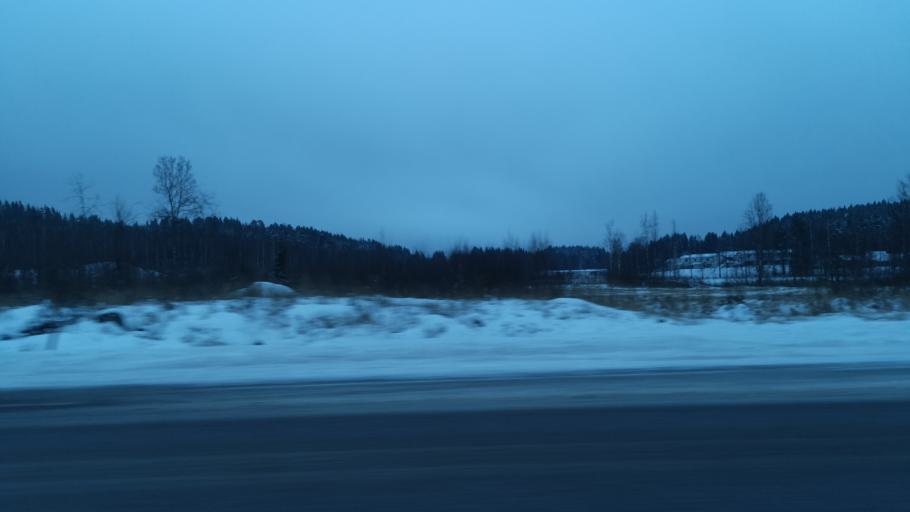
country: FI
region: Southern Savonia
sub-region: Savonlinna
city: Savonlinna
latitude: 61.8686
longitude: 28.9474
